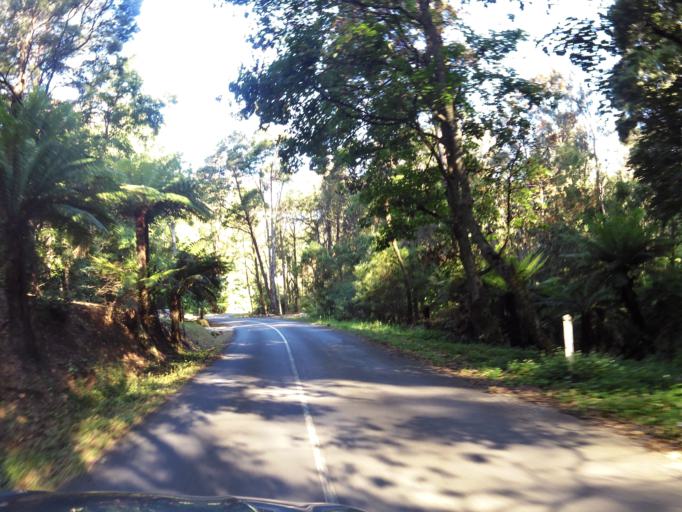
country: AU
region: Victoria
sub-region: Yarra Ranges
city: Olinda
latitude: -37.8657
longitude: 145.3566
